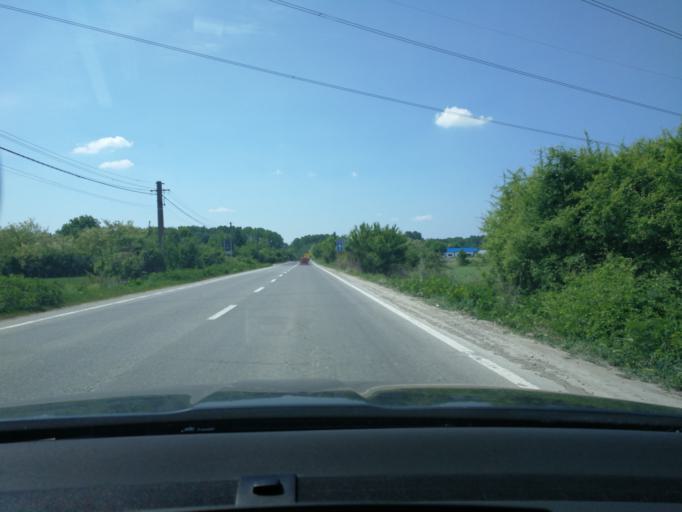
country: RO
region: Prahova
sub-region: Comuna Targsoru Vechi
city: Targsoru Vechi
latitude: 44.8584
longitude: 25.9250
